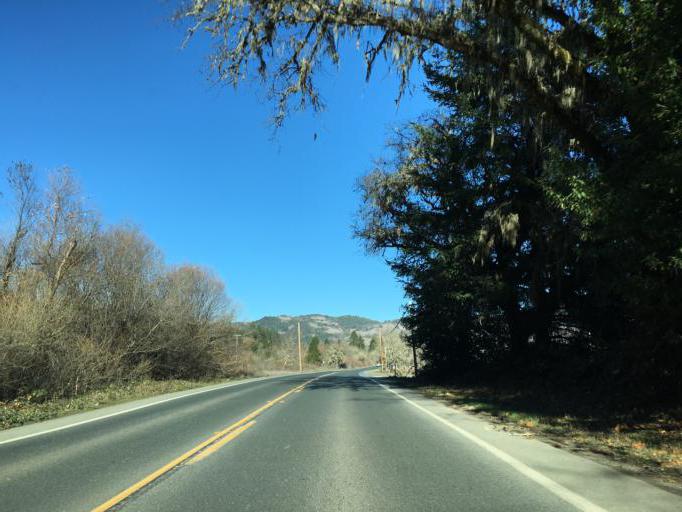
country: US
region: California
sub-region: Mendocino County
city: Brooktrails
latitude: 39.4411
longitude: -123.3551
